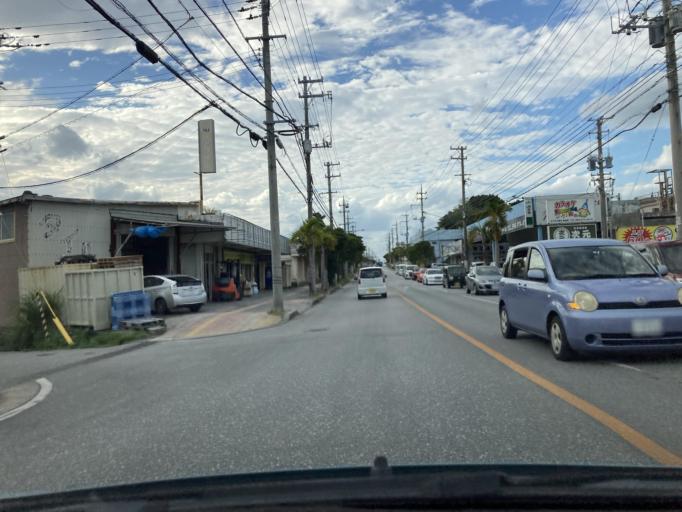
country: JP
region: Okinawa
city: Okinawa
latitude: 26.3568
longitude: 127.8288
